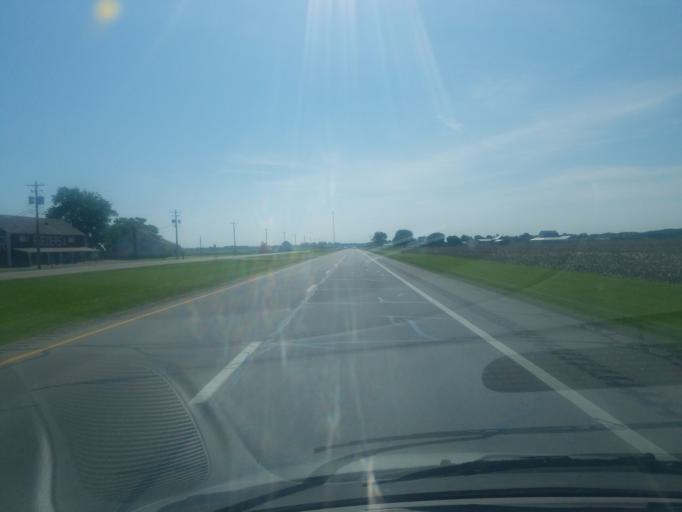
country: US
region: Ohio
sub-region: Huron County
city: Monroeville
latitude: 41.2528
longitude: -82.7255
